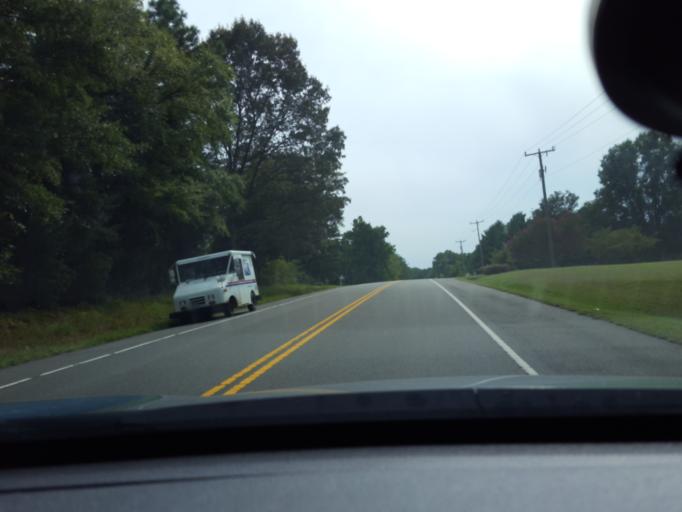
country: US
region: Virginia
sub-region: Hanover County
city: Hanover
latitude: 37.7185
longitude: -77.3740
